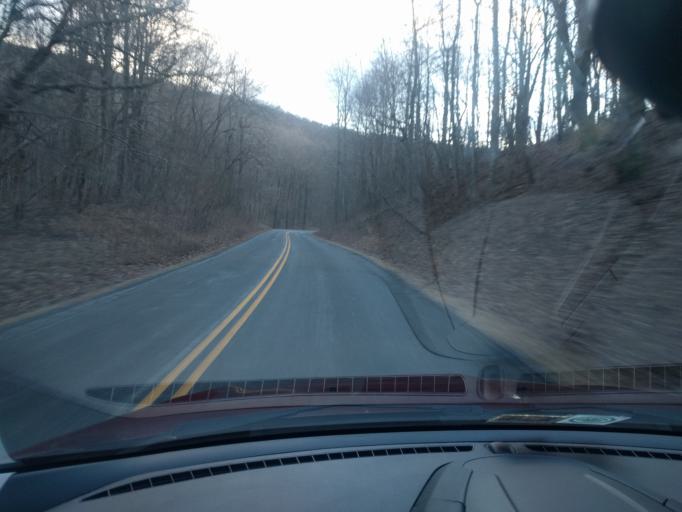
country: US
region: Virginia
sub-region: Botetourt County
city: Buchanan
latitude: 37.4554
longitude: -79.6272
